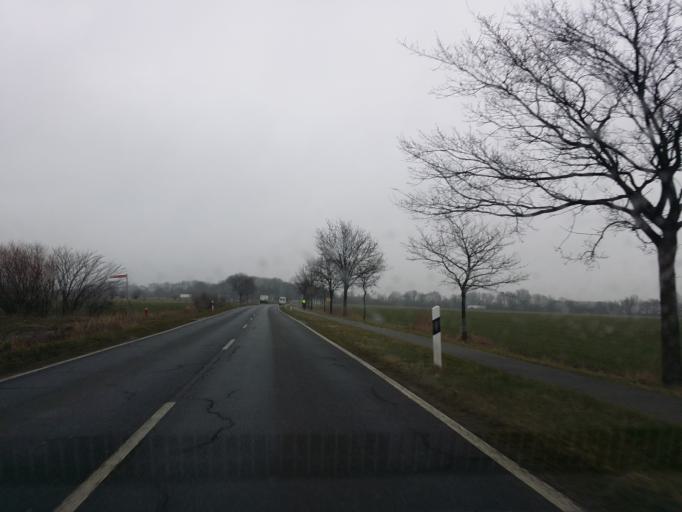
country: DE
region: Schleswig-Holstein
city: Fehmarn
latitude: 54.4474
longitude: 11.1606
